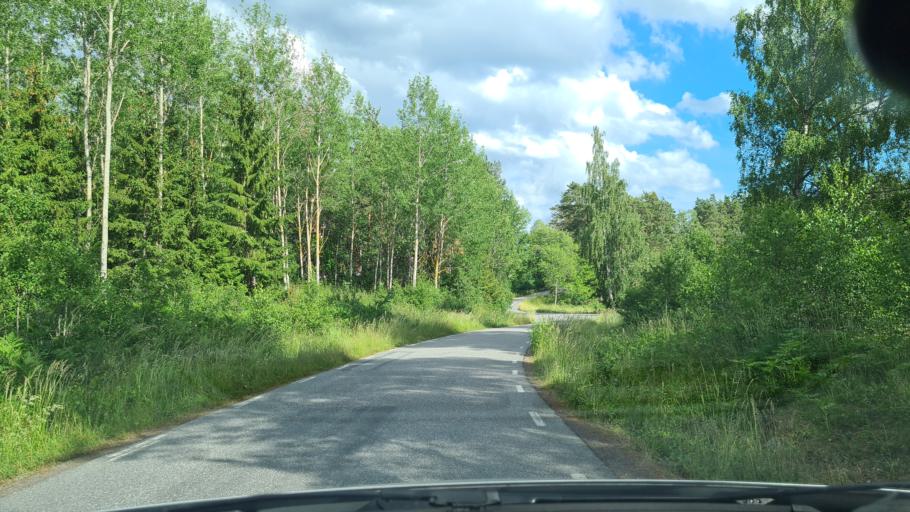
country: SE
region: Stockholm
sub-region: Varmdo Kommun
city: Mortnas
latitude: 59.4105
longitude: 18.4506
